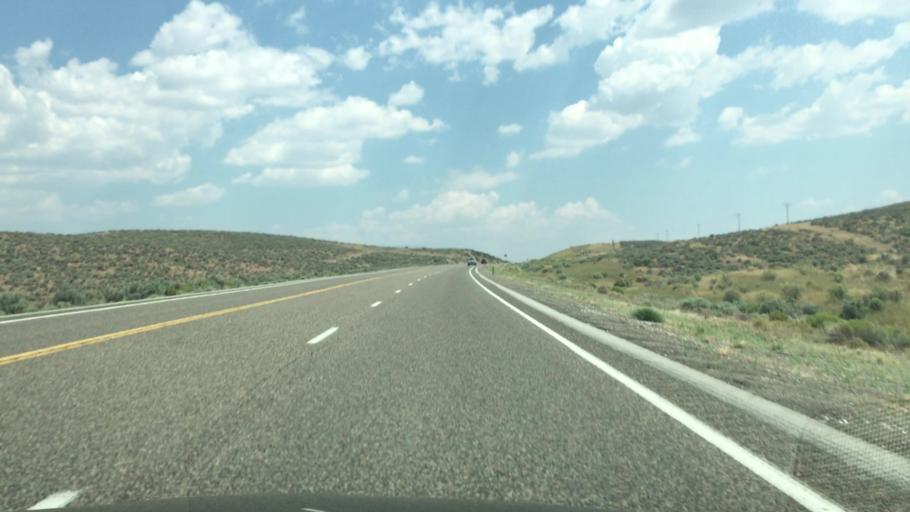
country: US
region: Nevada
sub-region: Elko County
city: Wells
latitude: 41.1872
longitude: -114.8733
